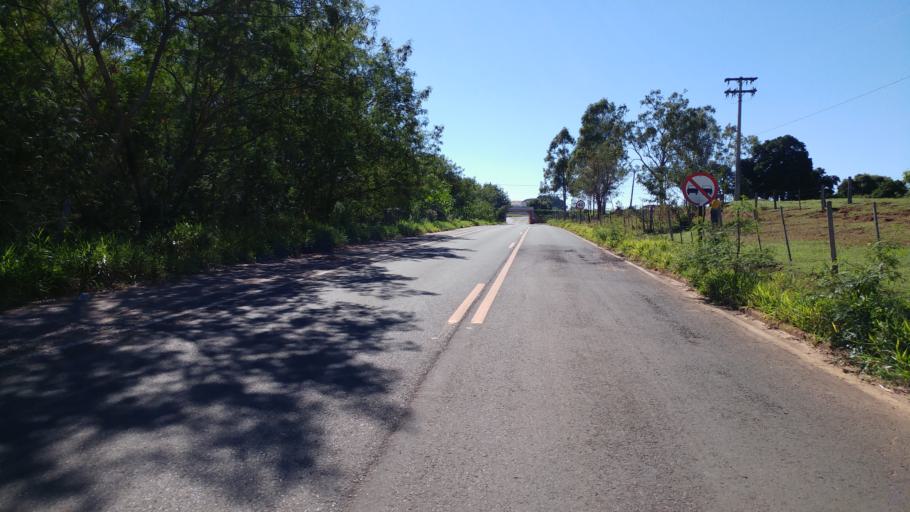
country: BR
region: Sao Paulo
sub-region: Paraguacu Paulista
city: Paraguacu Paulista
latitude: -22.4187
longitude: -50.5956
